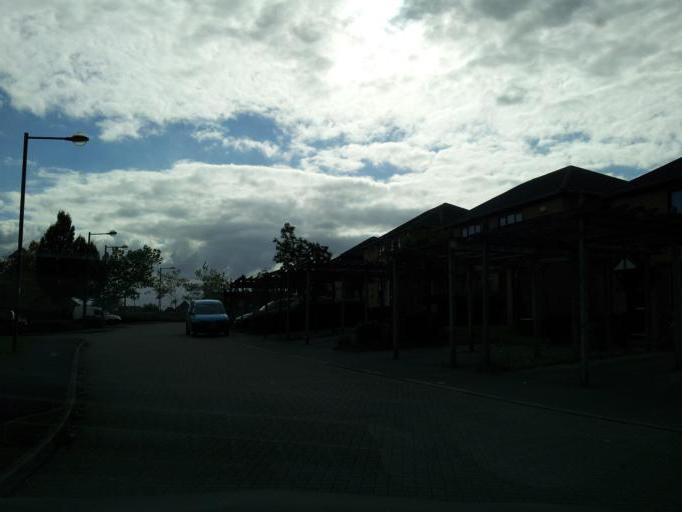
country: GB
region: England
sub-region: Milton Keynes
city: Shenley Church End
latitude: 52.0051
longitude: -0.7960
